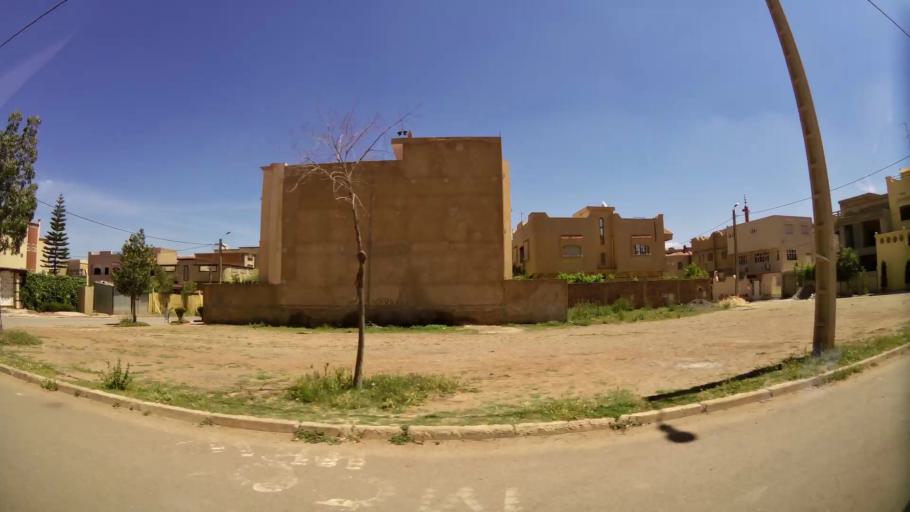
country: MA
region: Oriental
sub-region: Oujda-Angad
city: Oujda
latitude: 34.6619
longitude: -1.9451
